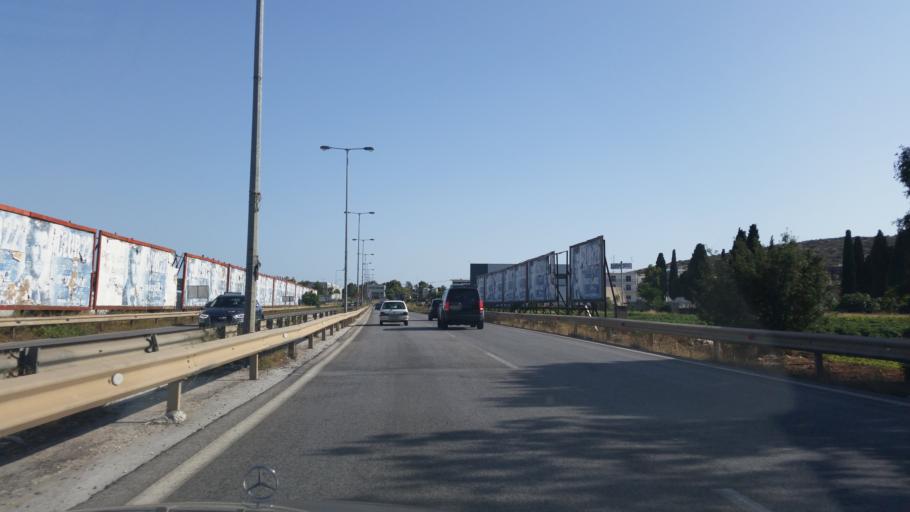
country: GR
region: Attica
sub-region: Nomarchia Anatolikis Attikis
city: Koropi
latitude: 37.8958
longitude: 23.8838
